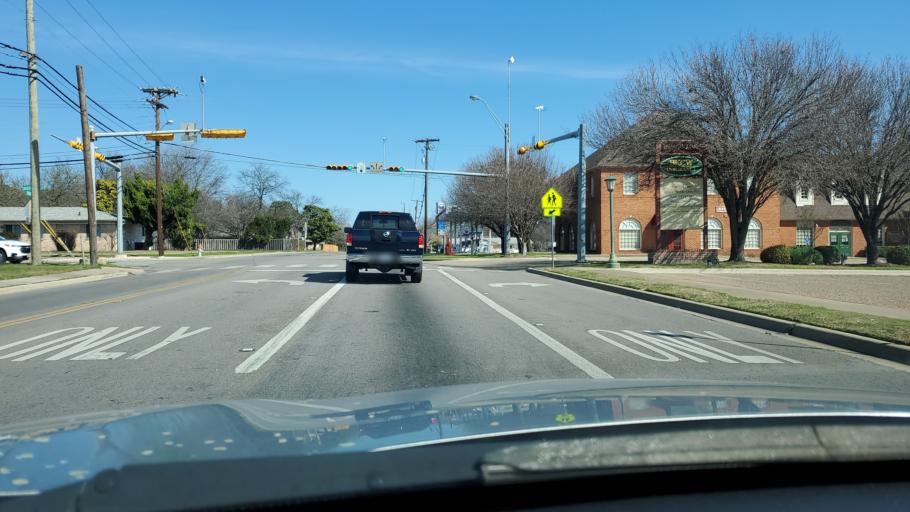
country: US
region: Texas
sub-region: Bell County
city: Killeen
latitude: 31.0978
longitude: -97.7312
